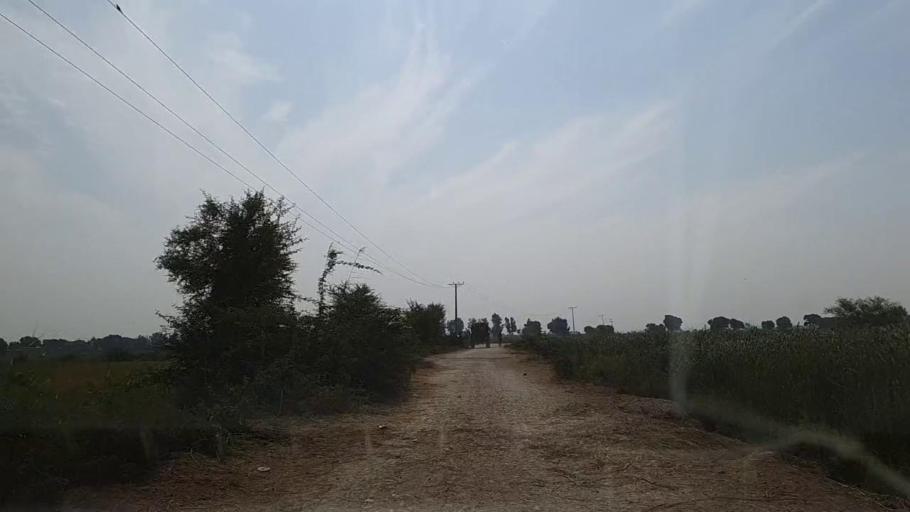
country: PK
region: Sindh
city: Mirpur Batoro
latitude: 24.6145
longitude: 68.2363
